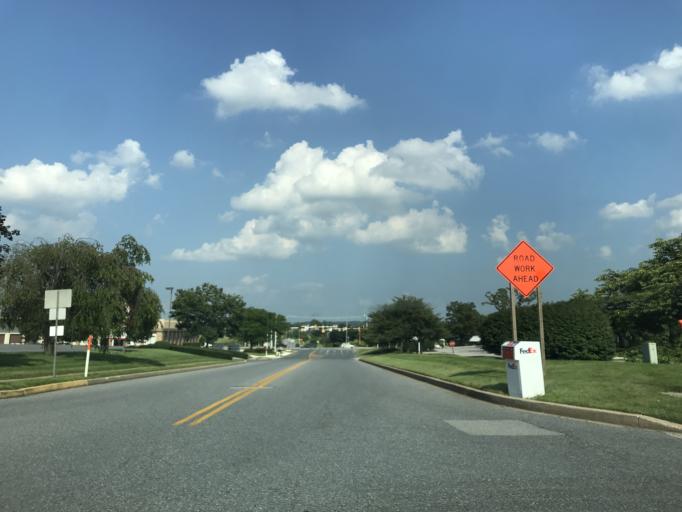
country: US
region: Maryland
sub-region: Carroll County
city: Westminster
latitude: 39.6067
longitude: -77.0003
